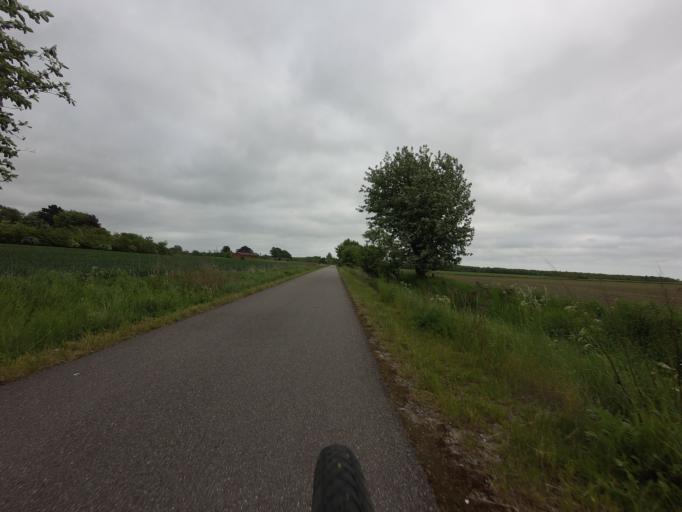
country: DK
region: Zealand
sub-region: Slagelse Kommune
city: Slagelse
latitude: 55.3048
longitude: 11.4151
